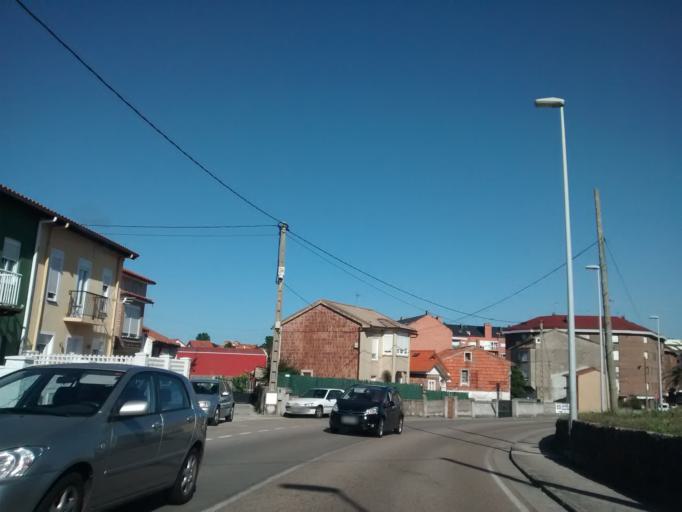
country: ES
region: Cantabria
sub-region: Provincia de Cantabria
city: Santander
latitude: 43.4655
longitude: -3.8439
